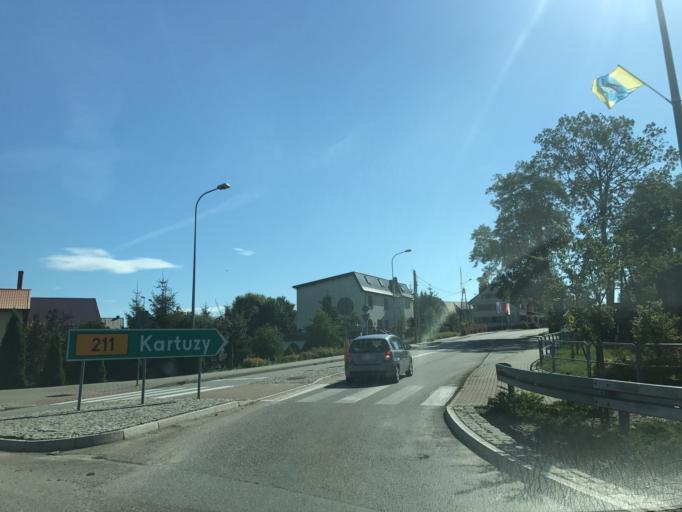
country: PL
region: Pomeranian Voivodeship
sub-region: Powiat bytowski
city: Czarna Dabrowka
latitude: 54.3561
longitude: 17.5647
